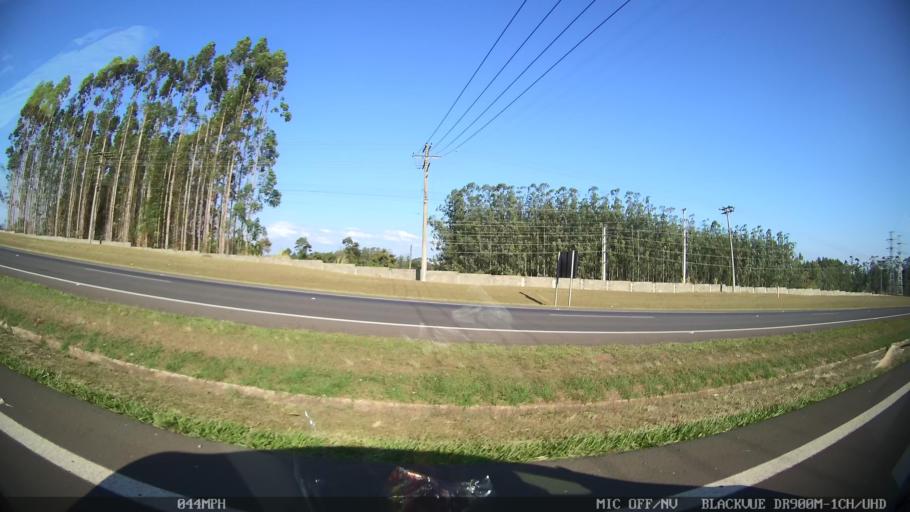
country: BR
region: Sao Paulo
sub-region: Piracicaba
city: Piracicaba
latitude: -22.6921
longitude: -47.6464
